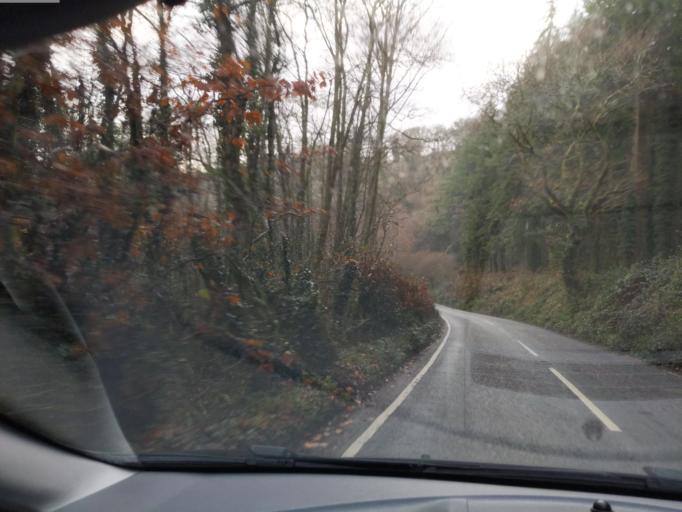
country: GB
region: England
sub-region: Cornwall
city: Looe
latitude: 50.3867
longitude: -4.3890
